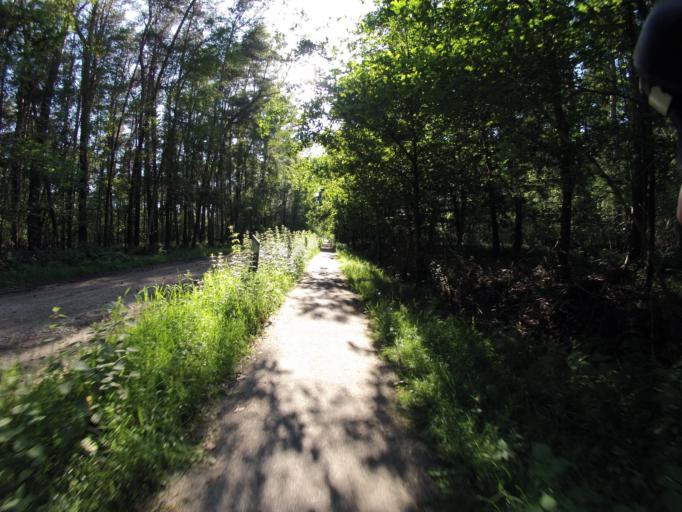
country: DE
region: Lower Saxony
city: Ohne
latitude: 52.3081
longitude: 7.2972
